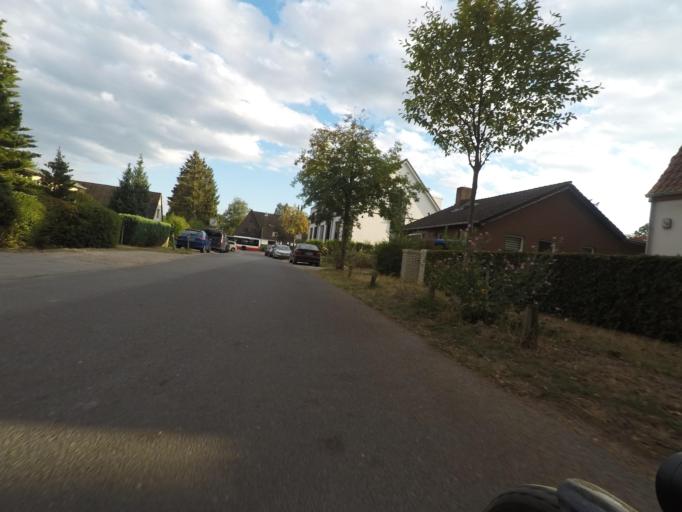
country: DE
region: Hamburg
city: Farmsen-Berne
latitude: 53.6216
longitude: 10.1022
